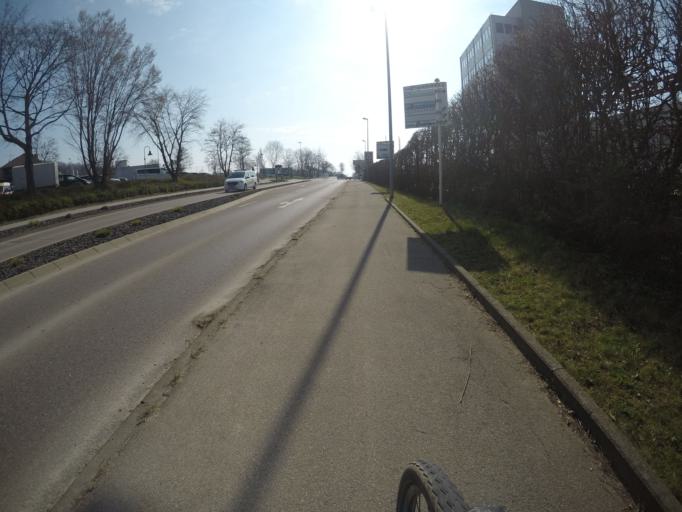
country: DE
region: Baden-Wuerttemberg
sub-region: Regierungsbezirk Stuttgart
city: Wolfschlugen
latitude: 48.6502
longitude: 9.2988
